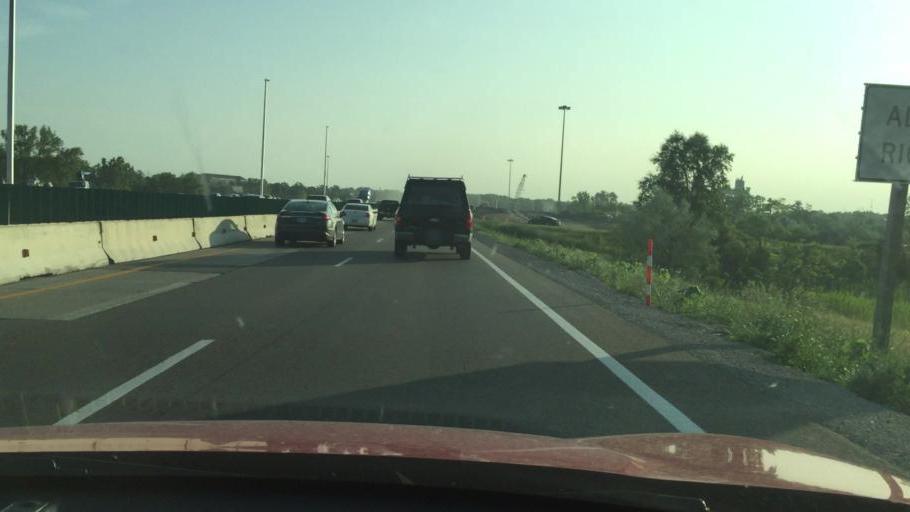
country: US
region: Michigan
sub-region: Genesee County
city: Flint
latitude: 42.9941
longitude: -83.7078
